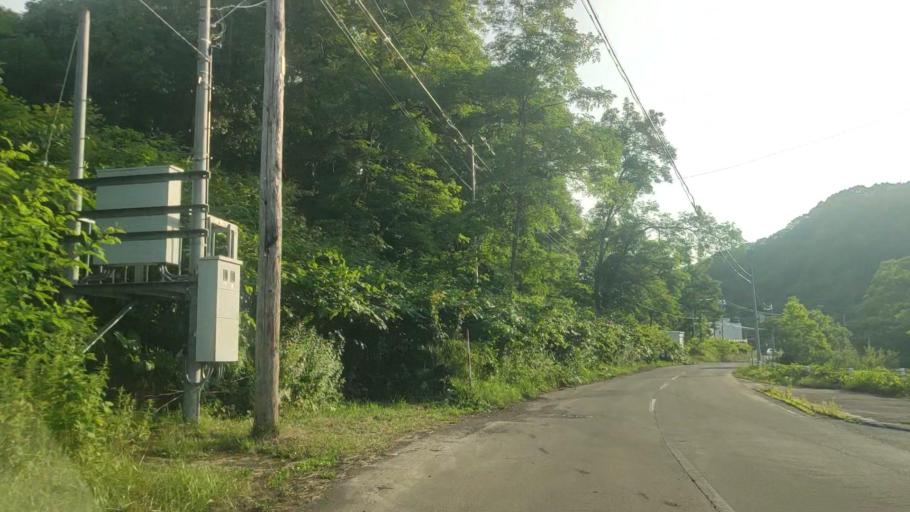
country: JP
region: Hokkaido
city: Iwamizawa
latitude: 43.0622
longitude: 141.9821
